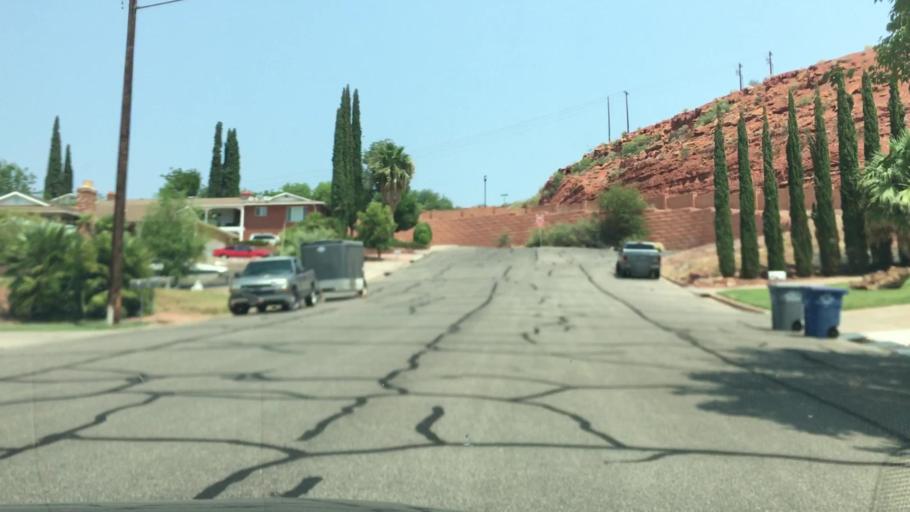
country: US
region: Utah
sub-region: Washington County
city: Saint George
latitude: 37.1140
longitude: -113.5812
